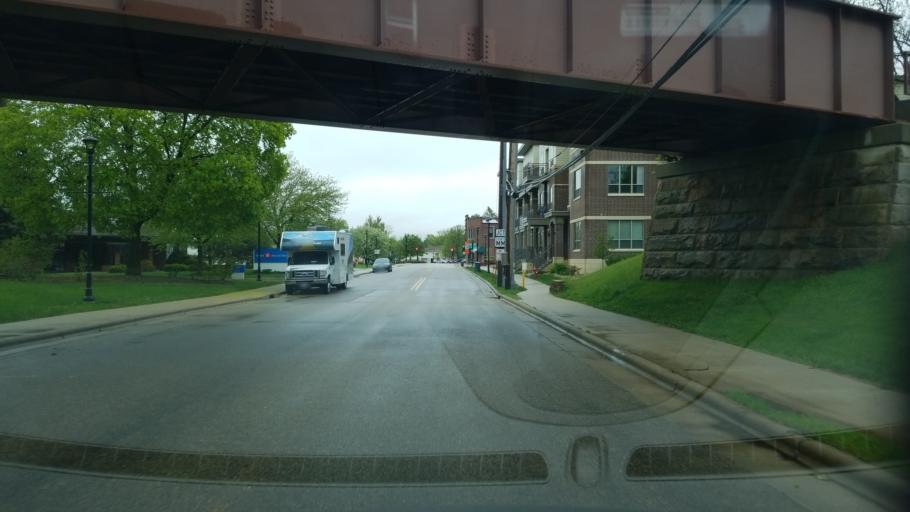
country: US
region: Wisconsin
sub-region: Dane County
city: Oregon
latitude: 42.9269
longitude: -89.3864
